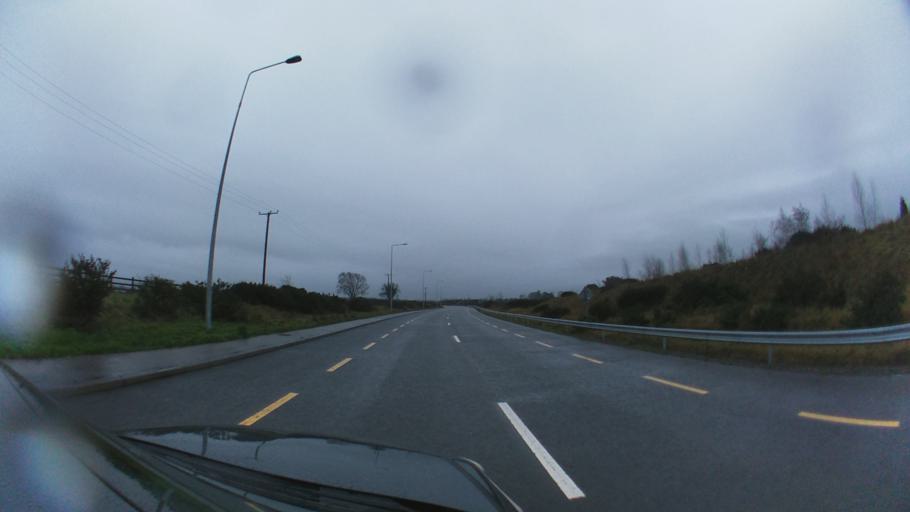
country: IE
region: Leinster
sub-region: County Carlow
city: Bagenalstown
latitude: 52.6785
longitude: -7.0327
